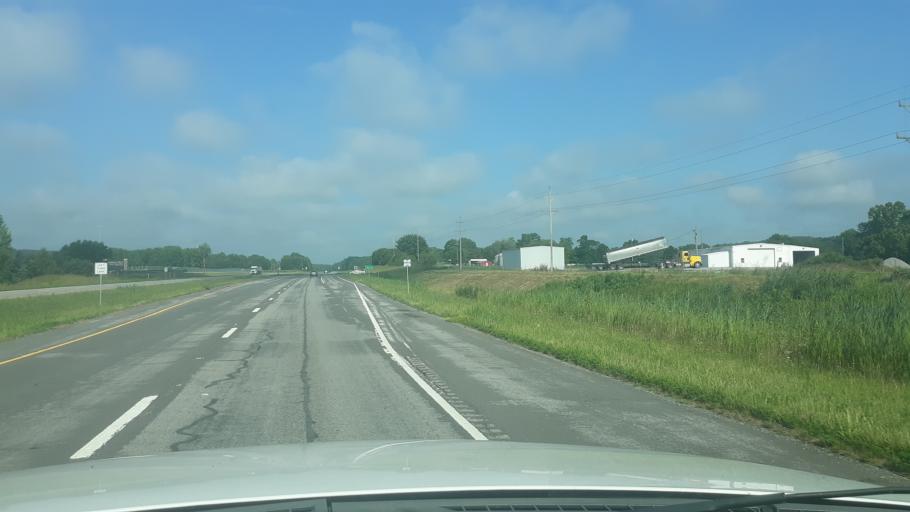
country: US
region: Illinois
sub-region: Saline County
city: Carrier Mills
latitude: 37.7335
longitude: -88.6707
